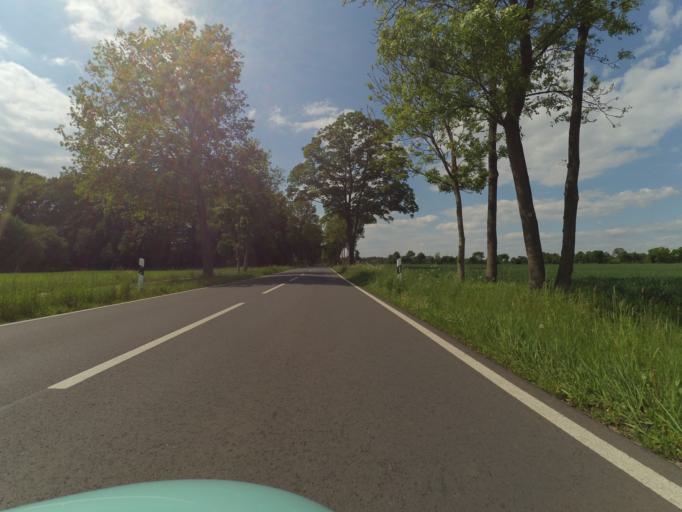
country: DE
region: Lower Saxony
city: Uetze
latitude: 52.4641
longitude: 10.2487
